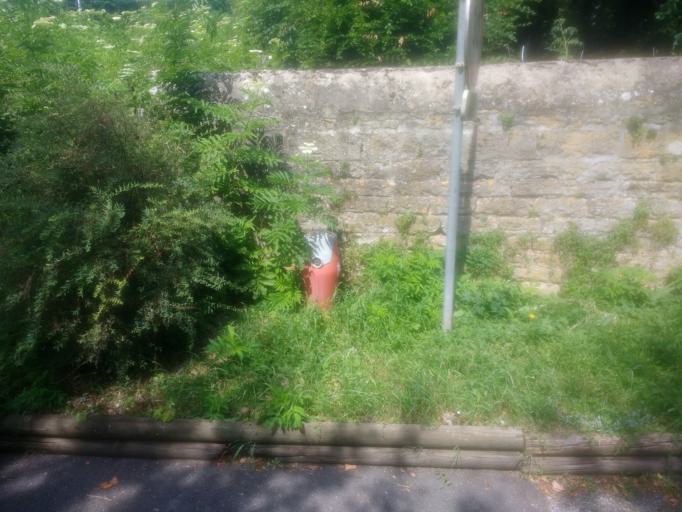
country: FR
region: Bourgogne
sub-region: Departement de Saone-et-Loire
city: Saint-Martin-Belle-Roche
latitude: 46.3667
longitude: 4.8562
